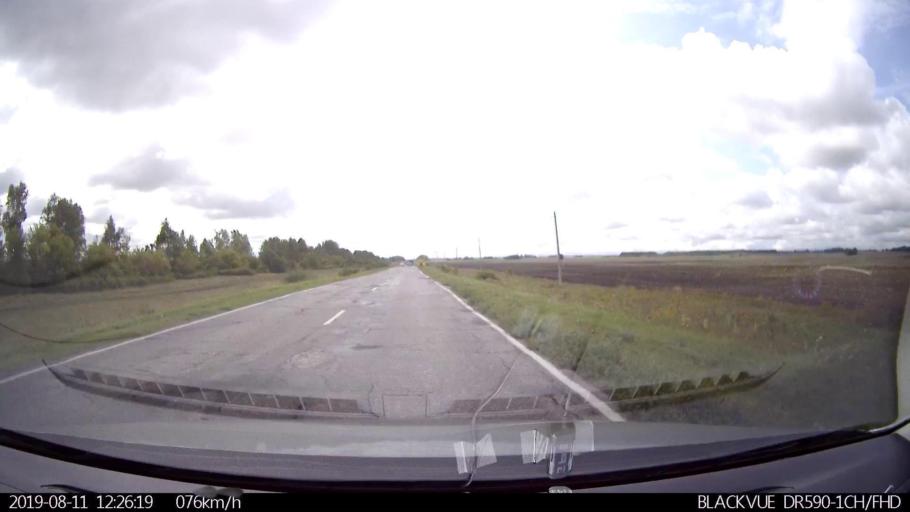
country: RU
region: Ulyanovsk
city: Ignatovka
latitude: 53.8650
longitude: 47.9316
